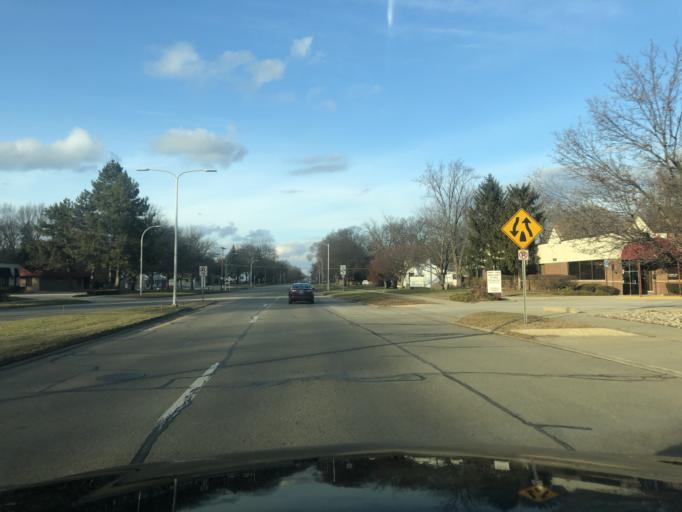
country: US
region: Michigan
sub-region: Wayne County
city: Livonia
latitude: 42.3994
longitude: -83.3736
